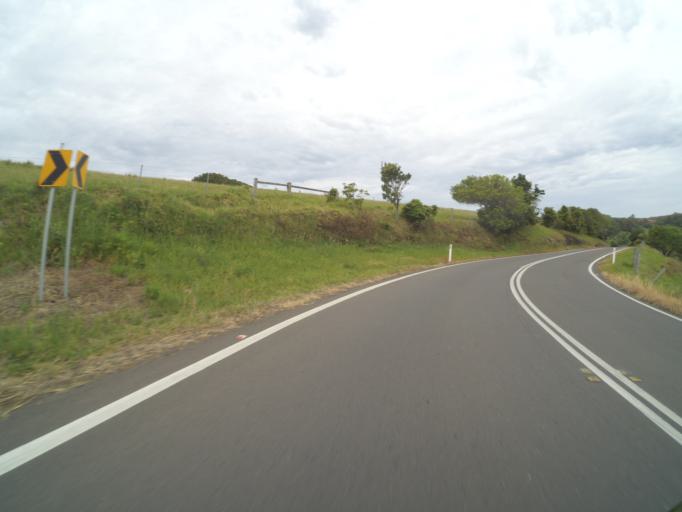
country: AU
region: New South Wales
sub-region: Kiama
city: Kiama
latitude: -34.6651
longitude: 150.8346
